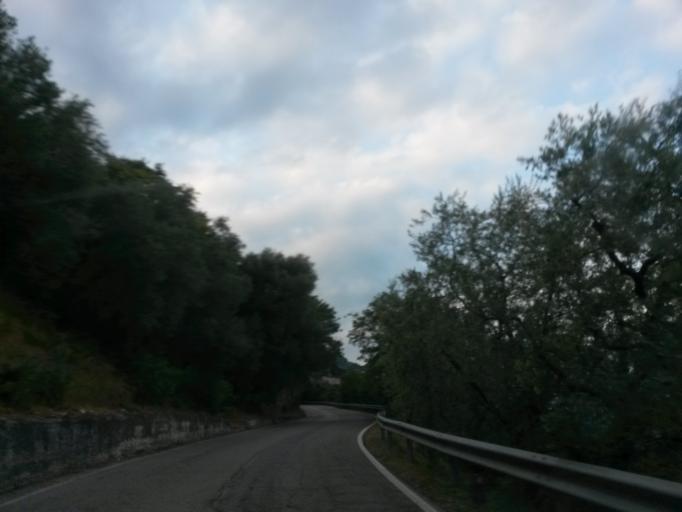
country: IT
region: Lombardy
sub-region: Provincia di Brescia
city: Gardola
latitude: 45.7204
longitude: 10.7068
